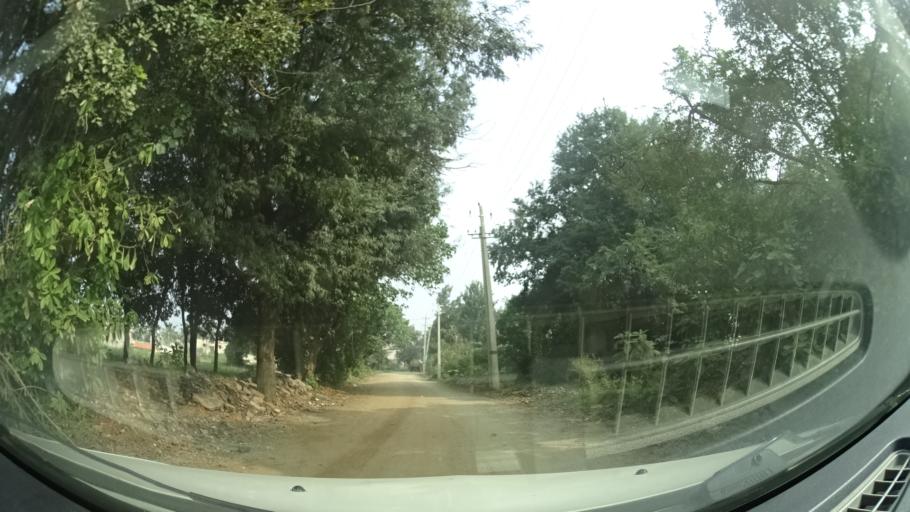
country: IN
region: Karnataka
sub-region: Bangalore Urban
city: Anekal
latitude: 12.7935
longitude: 77.6500
